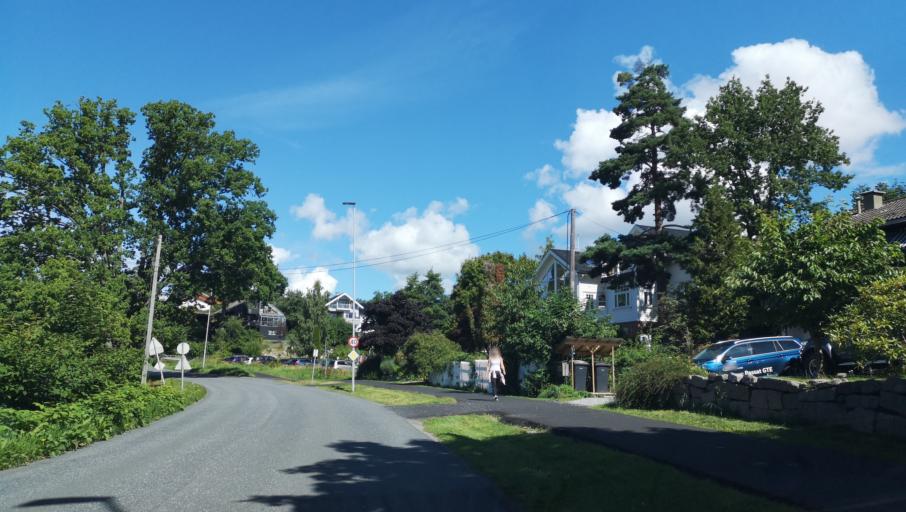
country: NO
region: Akershus
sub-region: Frogn
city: Drobak
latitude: 59.6565
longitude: 10.6418
